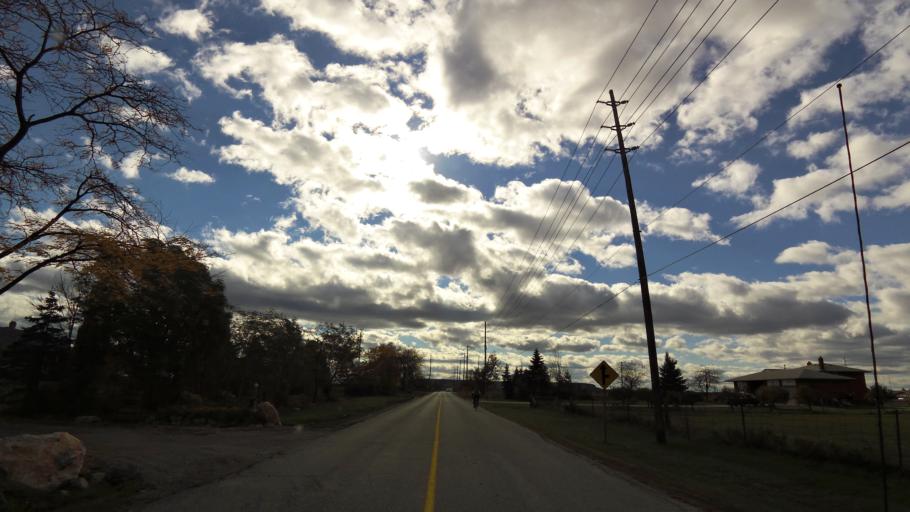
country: CA
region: Ontario
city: Burlington
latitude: 43.4589
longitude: -79.8166
